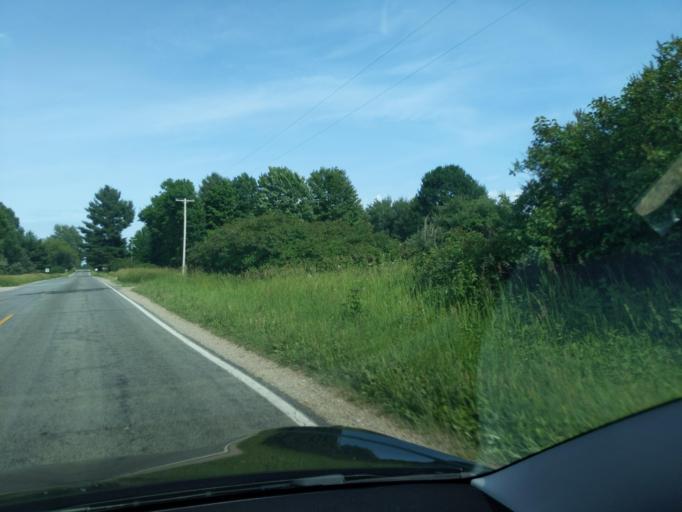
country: US
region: Michigan
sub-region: Newaygo County
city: Fremont
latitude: 43.4239
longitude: -85.9712
